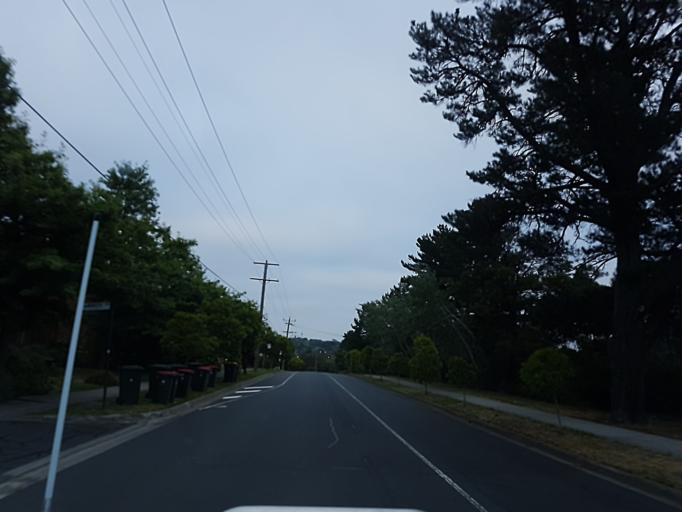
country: AU
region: Victoria
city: Burwood East
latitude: -37.8777
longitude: 145.1545
